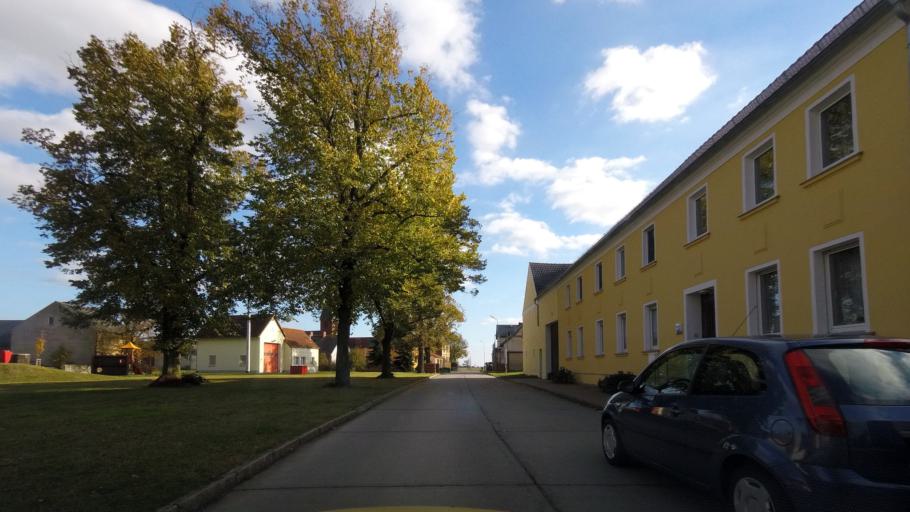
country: DE
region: Saxony-Anhalt
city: Seyda
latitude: 51.9481
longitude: 12.8674
